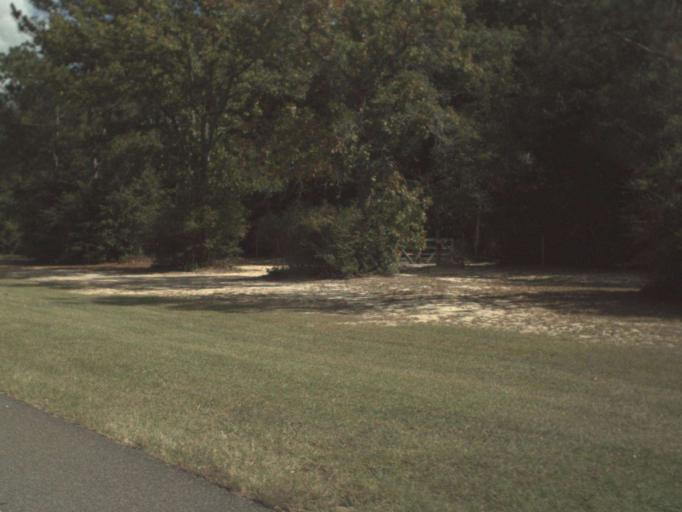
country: US
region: Florida
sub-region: Okaloosa County
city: Crestview
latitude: 30.6972
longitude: -86.7969
